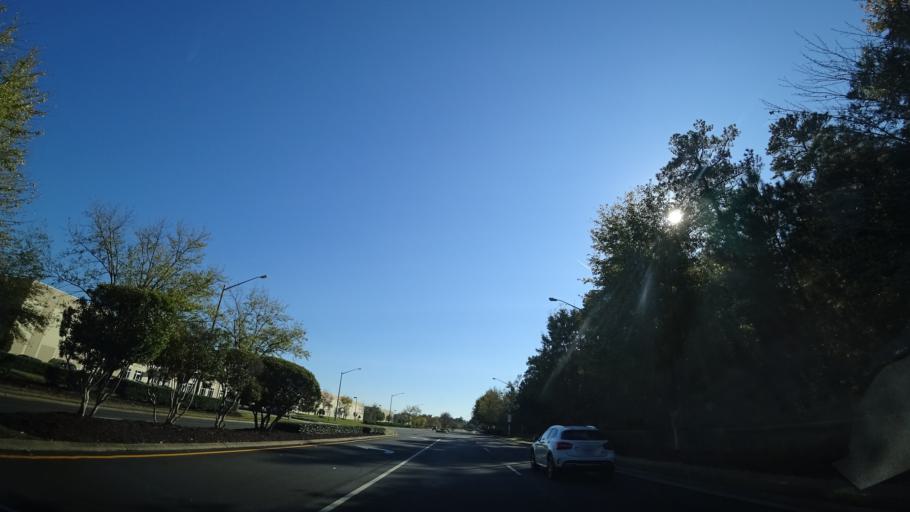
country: US
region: Virginia
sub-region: City of Newport News
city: Newport News
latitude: 36.8893
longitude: -76.4376
